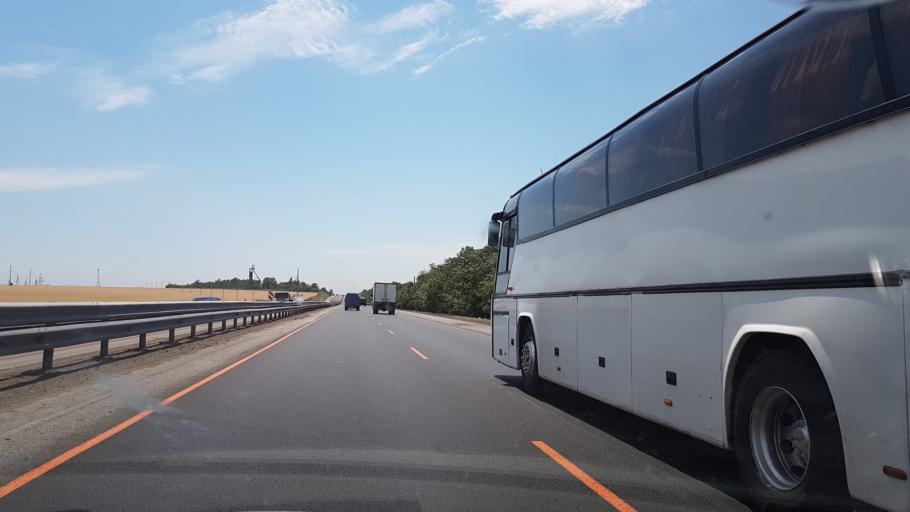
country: RU
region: Rostov
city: Ayutinskiy
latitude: 47.7828
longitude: 40.1622
